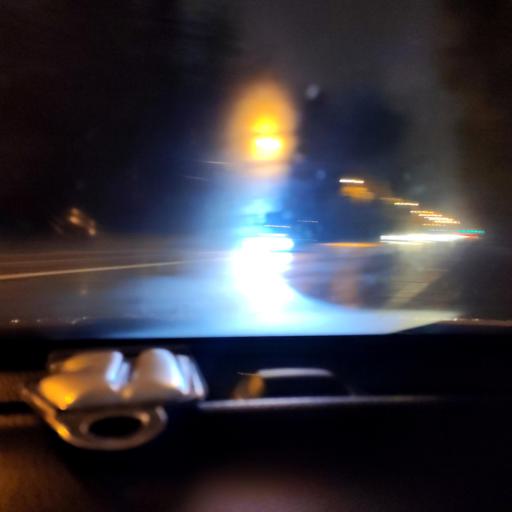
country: RU
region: Voronezj
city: Voronezh
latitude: 51.6841
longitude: 39.2826
